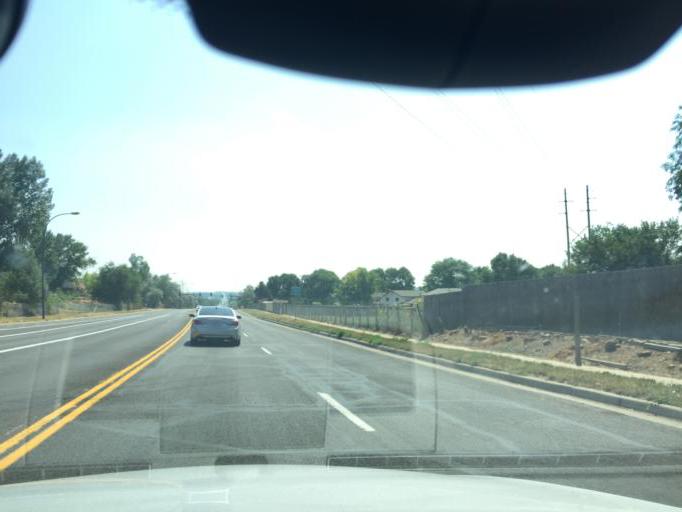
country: US
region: Colorado
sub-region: Broomfield County
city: Broomfield
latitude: 39.8998
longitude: -105.0713
